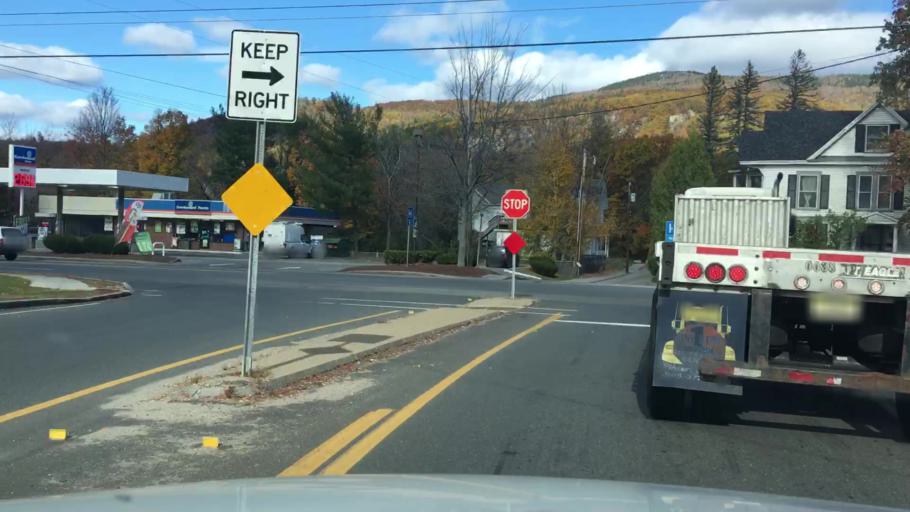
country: US
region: New Hampshire
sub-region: Coos County
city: Gorham
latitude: 44.3877
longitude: -71.1728
